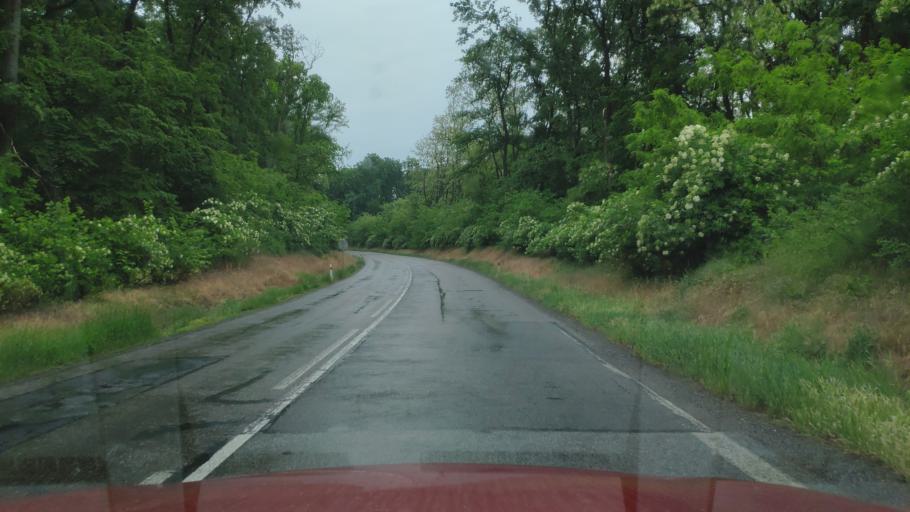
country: HU
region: Borsod-Abauj-Zemplen
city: Ricse
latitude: 48.4387
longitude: 21.9461
